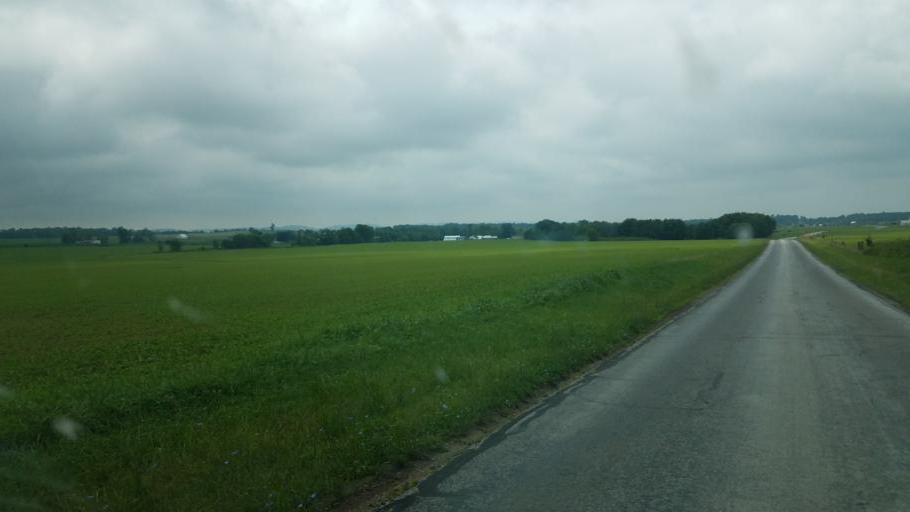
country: US
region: Ohio
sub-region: Highland County
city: Leesburg
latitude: 39.2419
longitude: -83.4878
